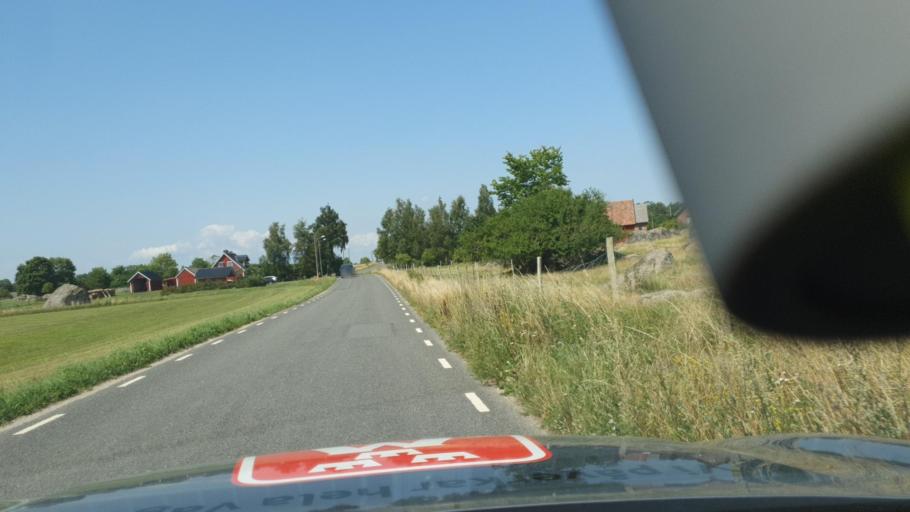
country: SE
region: Skane
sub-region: Kristianstads Kommun
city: Fjalkinge
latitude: 56.0671
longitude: 14.3628
